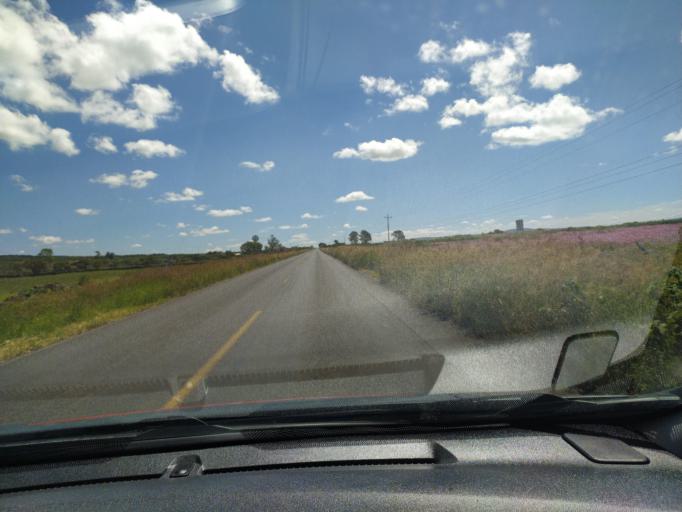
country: MX
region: Jalisco
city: Valle de Guadalupe
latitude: 21.0229
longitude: -102.5430
